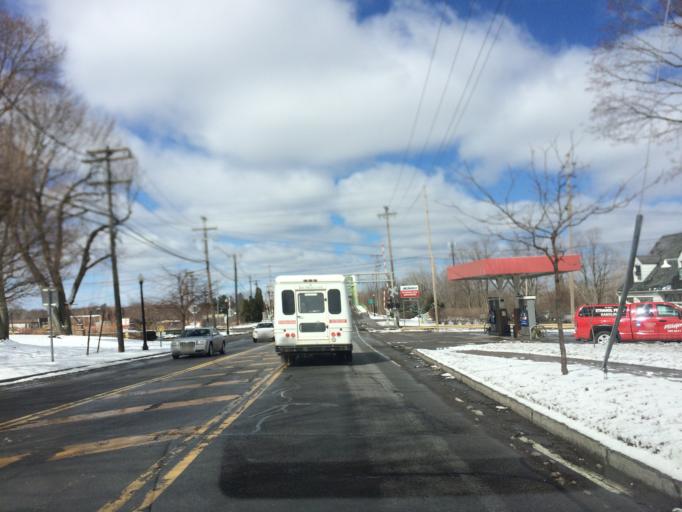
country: US
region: New York
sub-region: Monroe County
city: Pittsford
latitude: 43.0925
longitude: -77.5199
